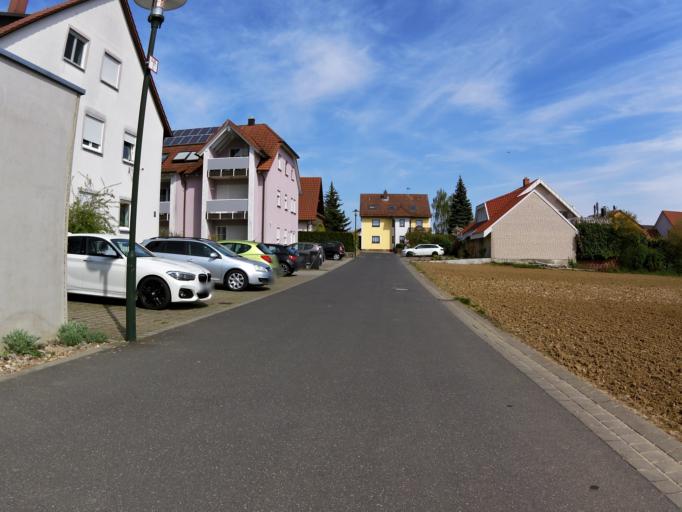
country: DE
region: Bavaria
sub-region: Regierungsbezirk Unterfranken
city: Unterpleichfeld
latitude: 49.8710
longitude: 10.0406
